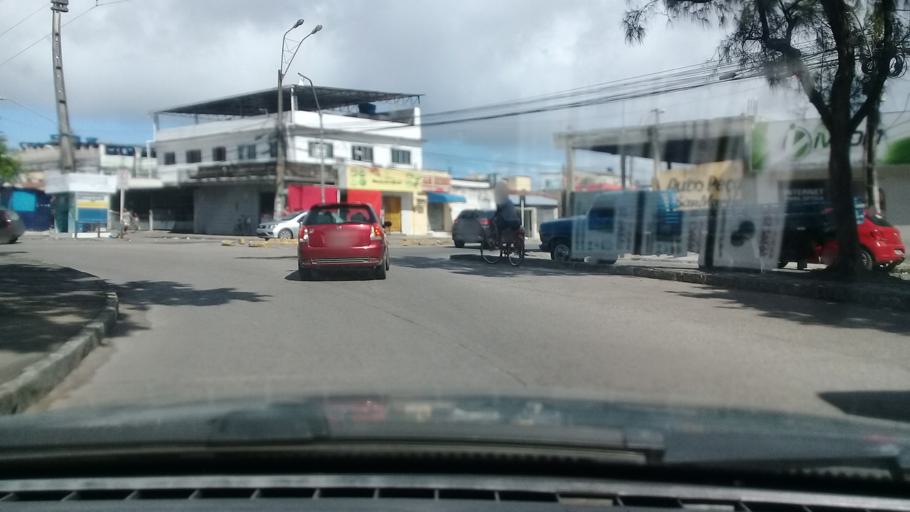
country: BR
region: Pernambuco
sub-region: Recife
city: Recife
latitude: -8.0711
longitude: -34.9291
